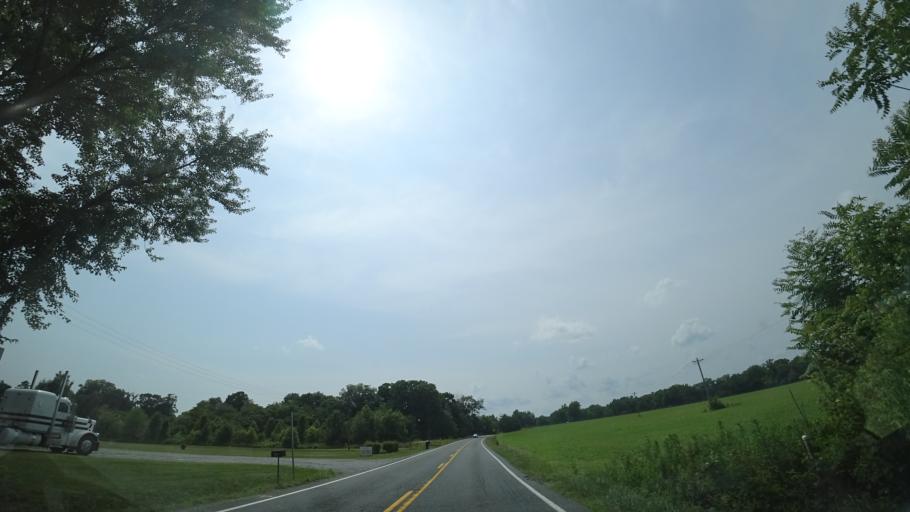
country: US
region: Virginia
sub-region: Spotsylvania County
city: Spotsylvania Courthouse
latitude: 38.1342
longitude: -77.5264
